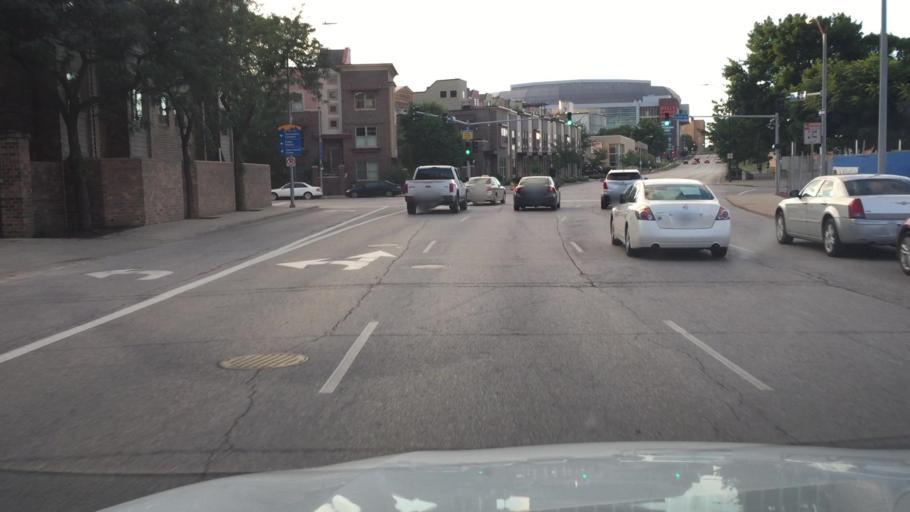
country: US
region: Iowa
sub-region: Polk County
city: Des Moines
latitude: 41.5883
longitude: -93.6203
